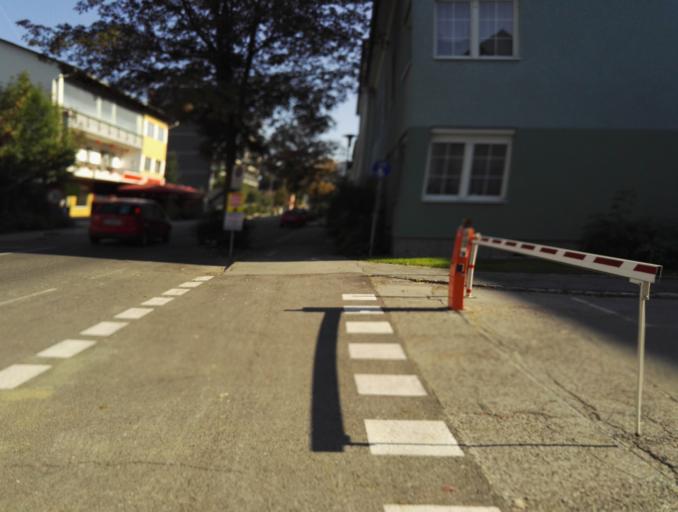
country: AT
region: Styria
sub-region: Politischer Bezirk Graz-Umgebung
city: Gratkorn
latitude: 47.1338
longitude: 15.3375
